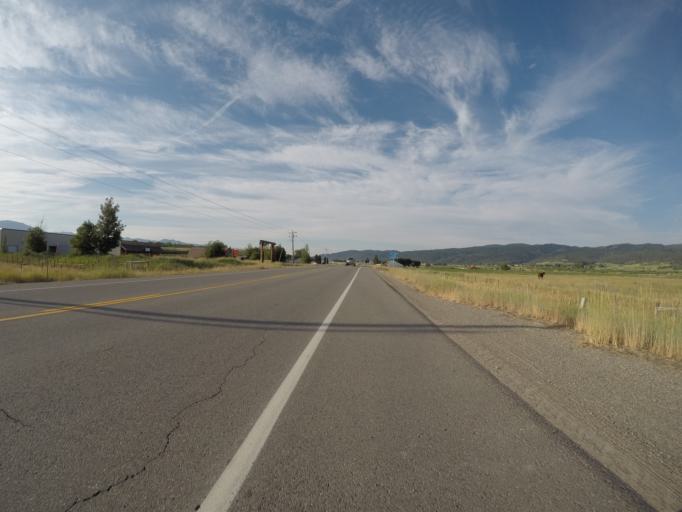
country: US
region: Wyoming
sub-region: Lincoln County
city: Afton
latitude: 42.9398
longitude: -111.0074
